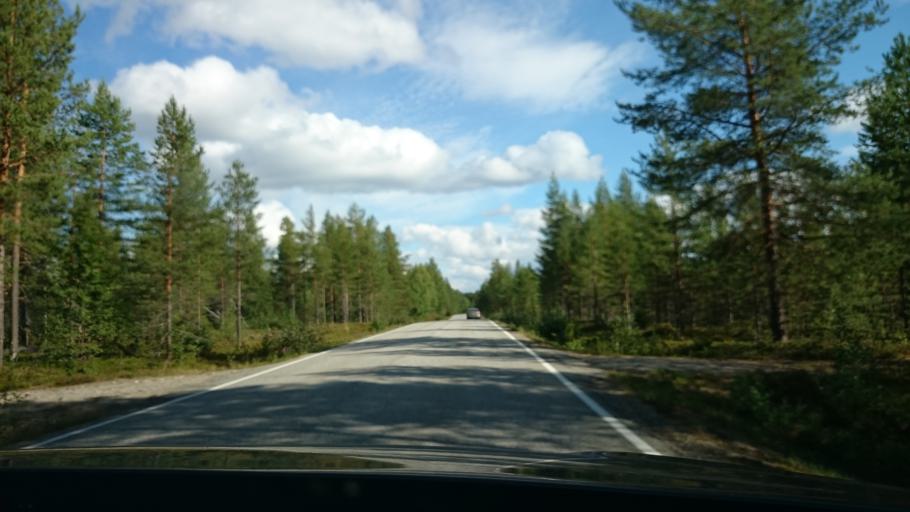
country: FI
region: Kainuu
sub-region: Kehys-Kainuu
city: Suomussalmi
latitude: 64.7508
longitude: 29.4250
